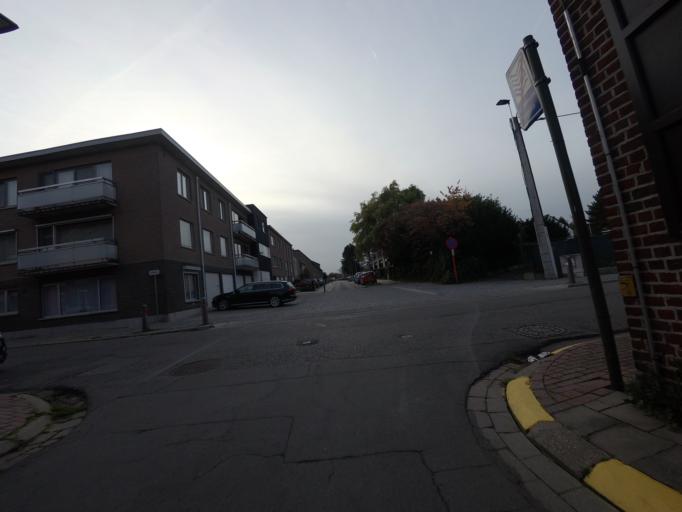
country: BE
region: Flanders
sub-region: Provincie Vlaams-Brabant
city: Herent
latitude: 50.9092
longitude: 4.6741
